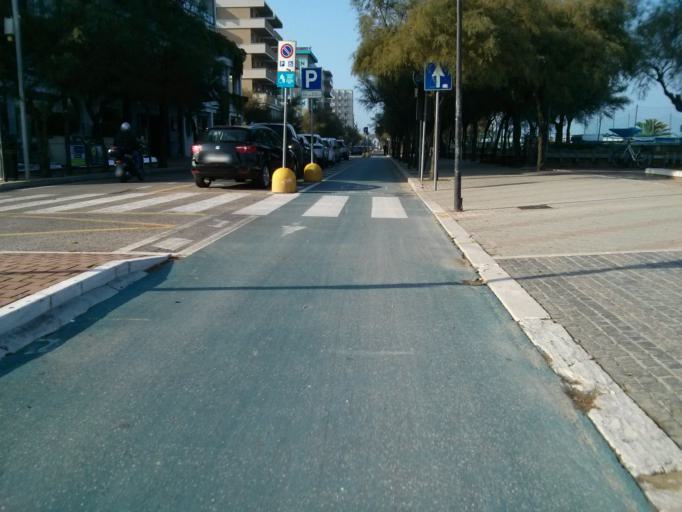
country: IT
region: The Marches
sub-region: Provincia di Pesaro e Urbino
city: Pesaro
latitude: 43.9161
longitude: 12.9147
